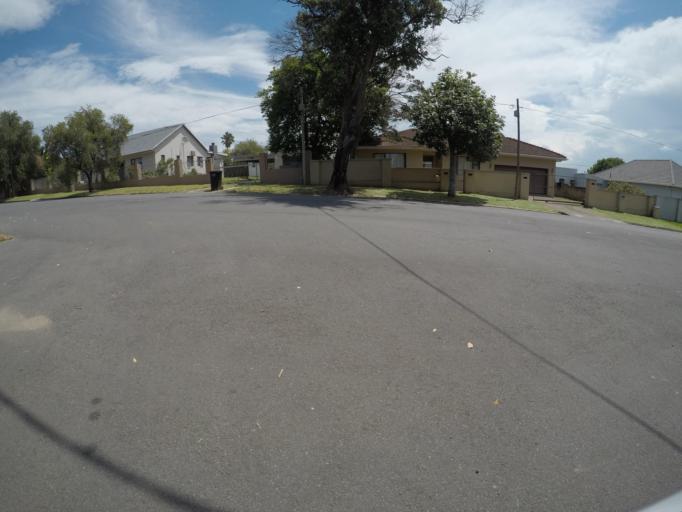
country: ZA
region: Eastern Cape
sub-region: Buffalo City Metropolitan Municipality
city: East London
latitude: -33.0323
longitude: 27.8599
